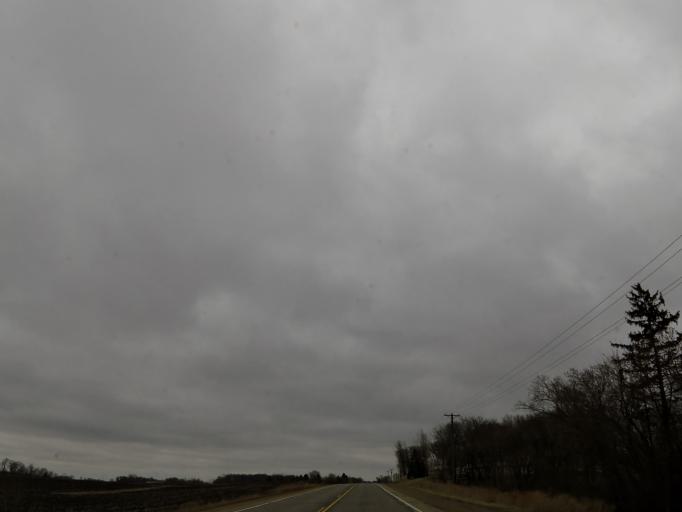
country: US
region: Minnesota
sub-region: Scott County
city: Shakopee
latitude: 44.7115
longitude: -93.5210
